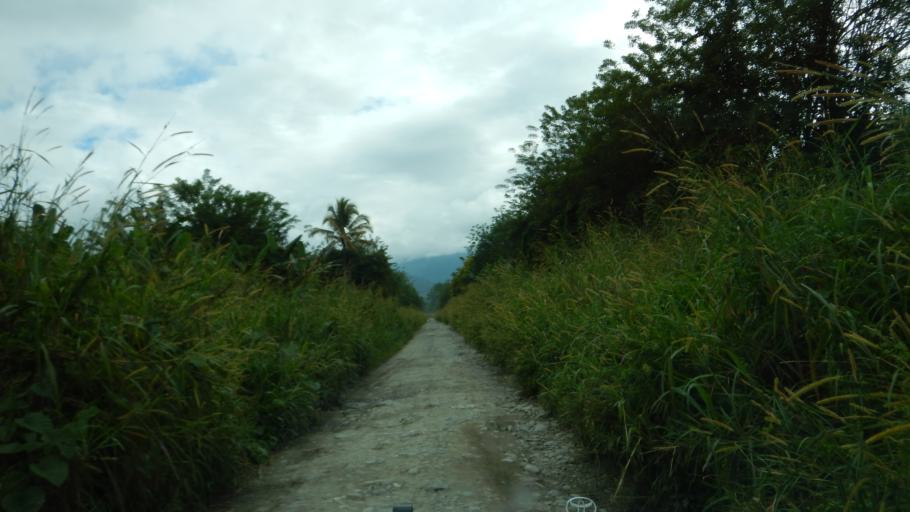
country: PG
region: Northern Province
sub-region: Sohe
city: Kokoda
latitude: -8.9079
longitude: 147.7982
